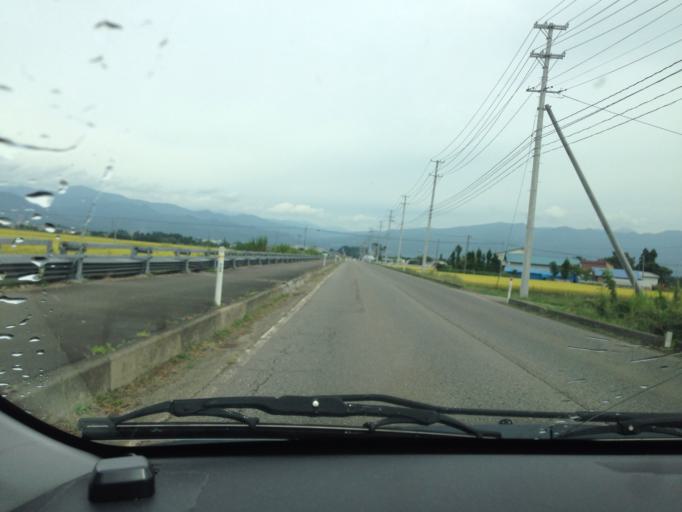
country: JP
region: Fukushima
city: Kitakata
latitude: 37.6353
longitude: 139.8445
